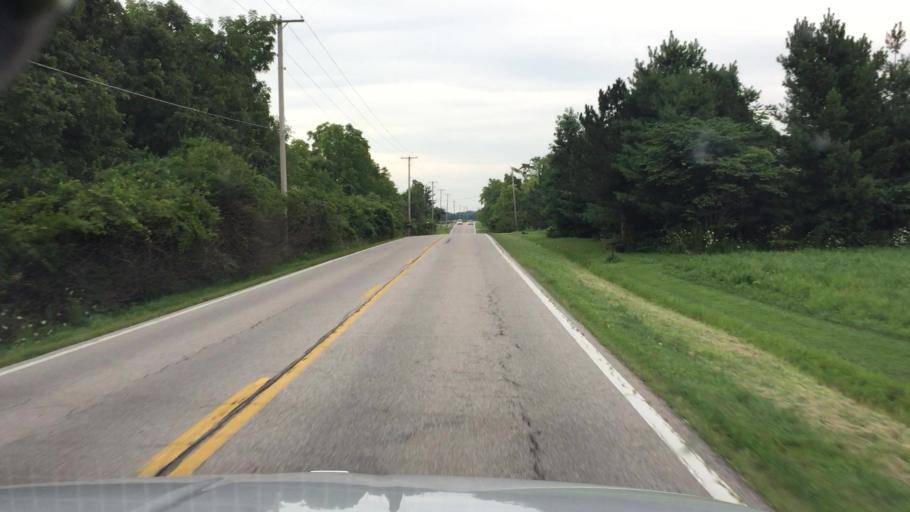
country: US
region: Ohio
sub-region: Madison County
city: Plain City
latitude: 40.0506
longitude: -83.2606
